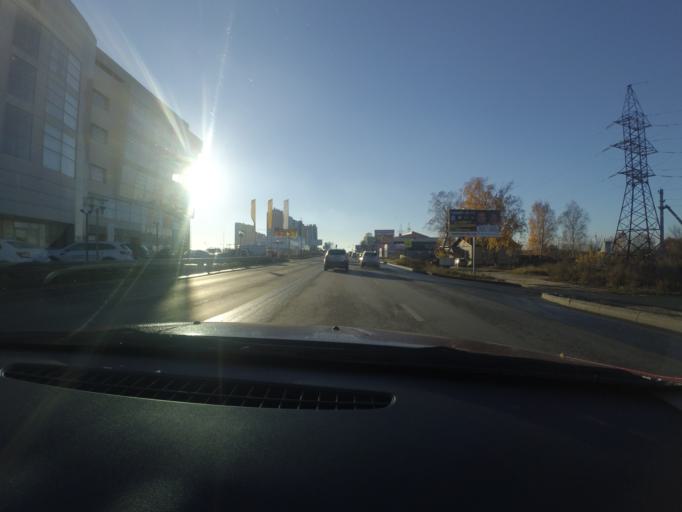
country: RU
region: Nizjnij Novgorod
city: Afonino
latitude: 56.2815
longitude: 44.0801
